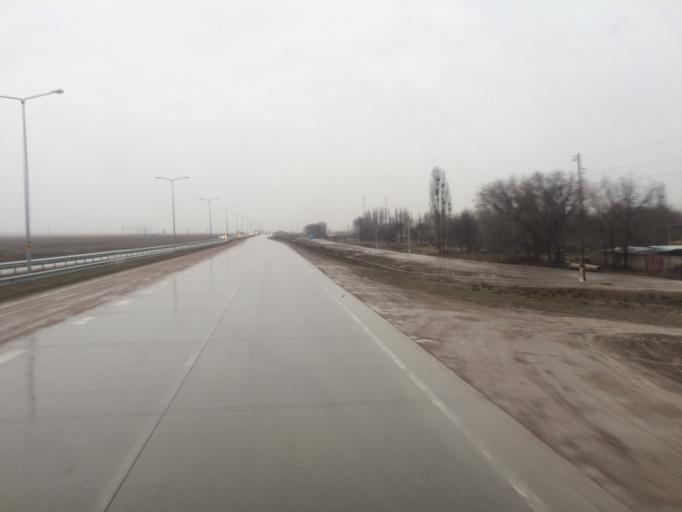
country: KZ
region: Zhambyl
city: Merke
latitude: 42.8886
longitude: 72.9943
